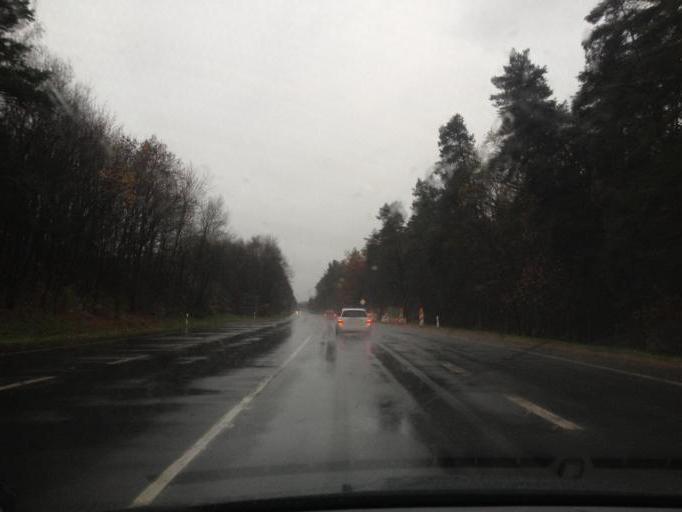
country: DE
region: Bavaria
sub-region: Regierungsbezirk Mittelfranken
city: Ruckersdorf
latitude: 49.4960
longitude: 11.2590
